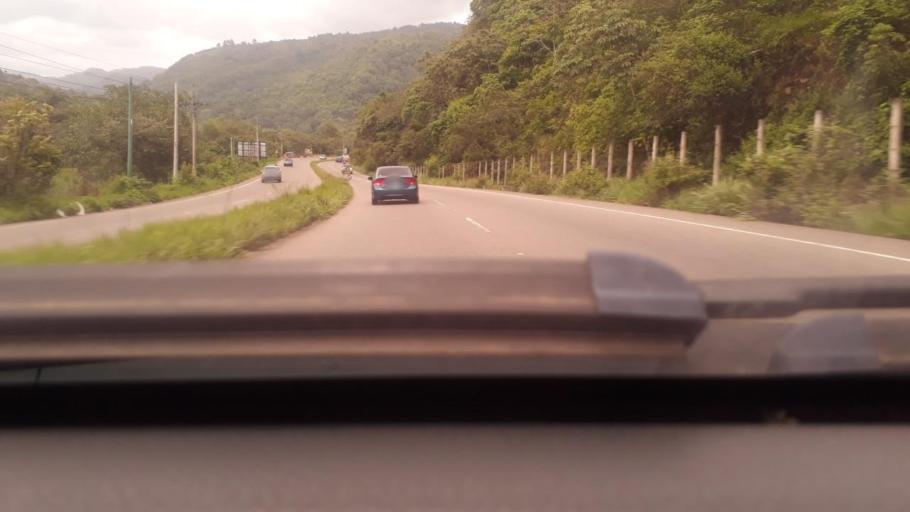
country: GT
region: Santa Rosa
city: Oratorio
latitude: 14.2561
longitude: -90.2182
